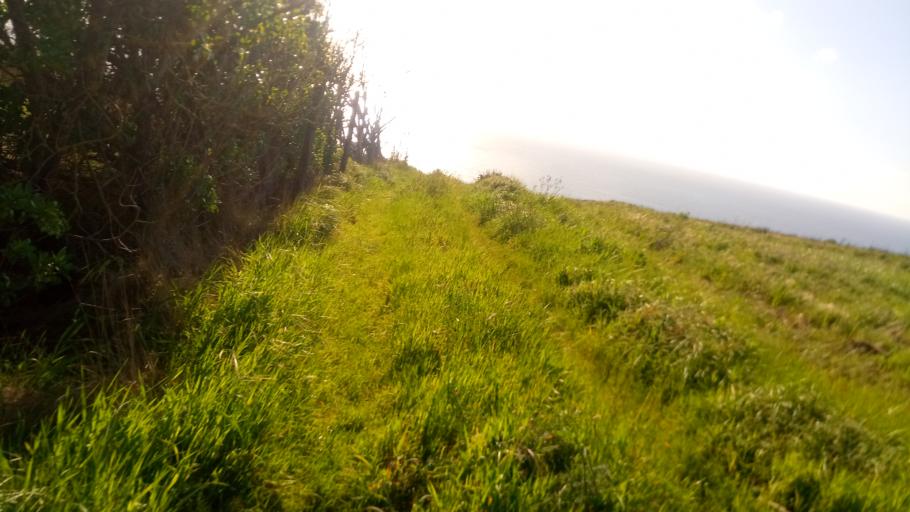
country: PT
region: Leiria
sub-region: Caldas da Rainha
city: Caldas da Rainha
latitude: 39.4633
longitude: -9.2005
